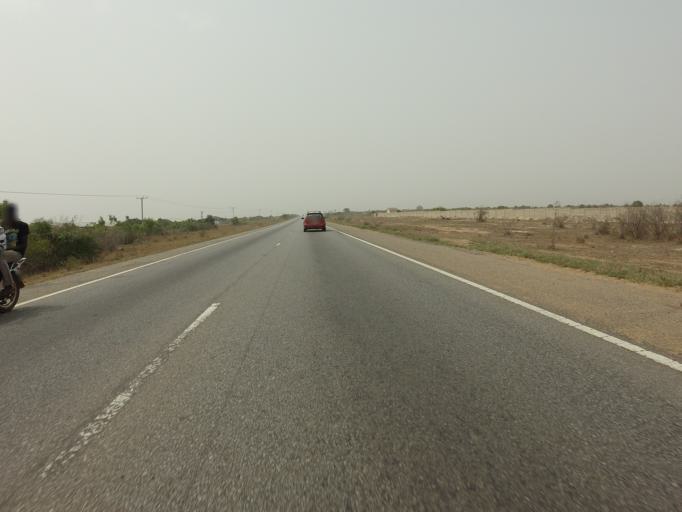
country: GH
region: Greater Accra
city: Tema
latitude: 5.8620
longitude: 0.2805
